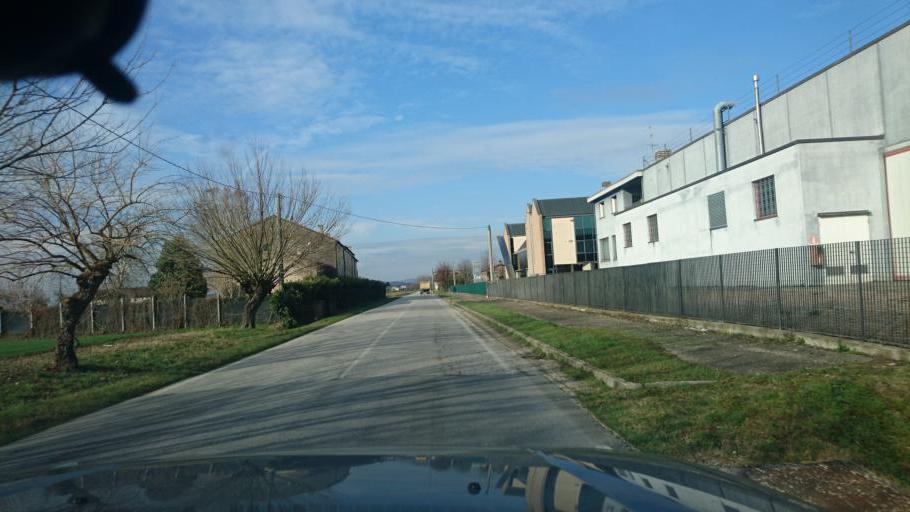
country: IT
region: Veneto
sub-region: Provincia di Padova
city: Bastia
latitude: 45.3813
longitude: 11.6449
